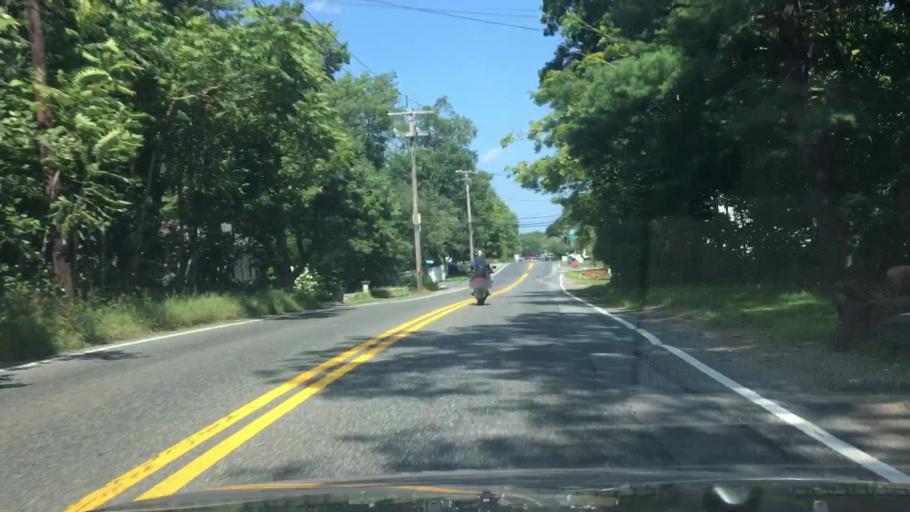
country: US
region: Massachusetts
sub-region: Middlesex County
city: Holliston
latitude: 42.1822
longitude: -71.4459
